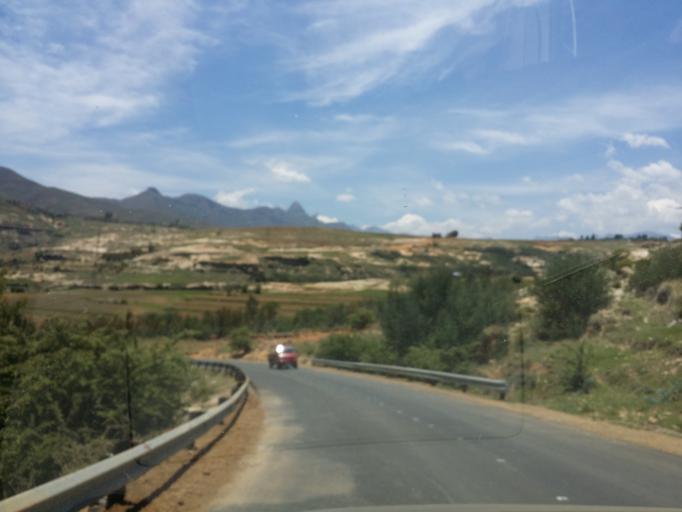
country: LS
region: Butha-Buthe
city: Butha-Buthe
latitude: -28.7365
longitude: 28.4336
